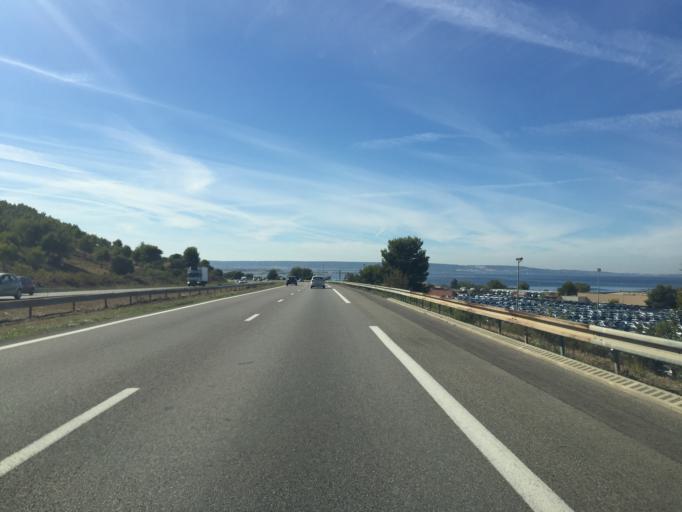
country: FR
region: Provence-Alpes-Cote d'Azur
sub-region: Departement des Bouches-du-Rhone
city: Rognac
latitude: 43.4762
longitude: 5.2371
